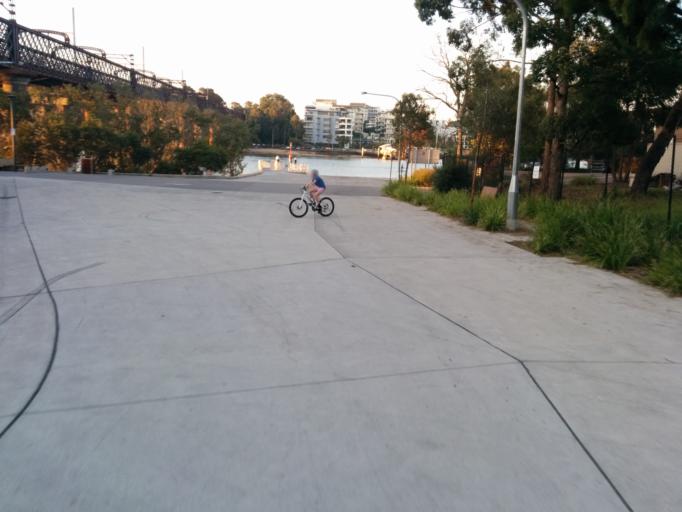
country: AU
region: New South Wales
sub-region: Canada Bay
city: Rhodes
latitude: -33.8235
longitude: 151.0890
